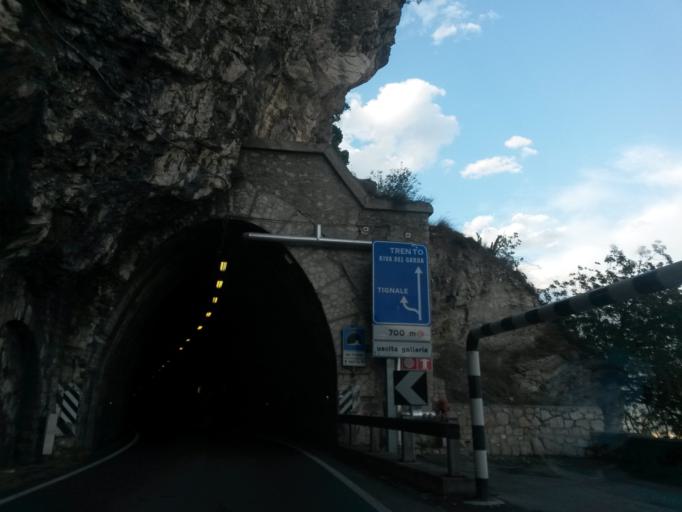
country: IT
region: Lombardy
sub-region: Provincia di Brescia
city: Gardola
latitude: 45.7087
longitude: 10.6938
